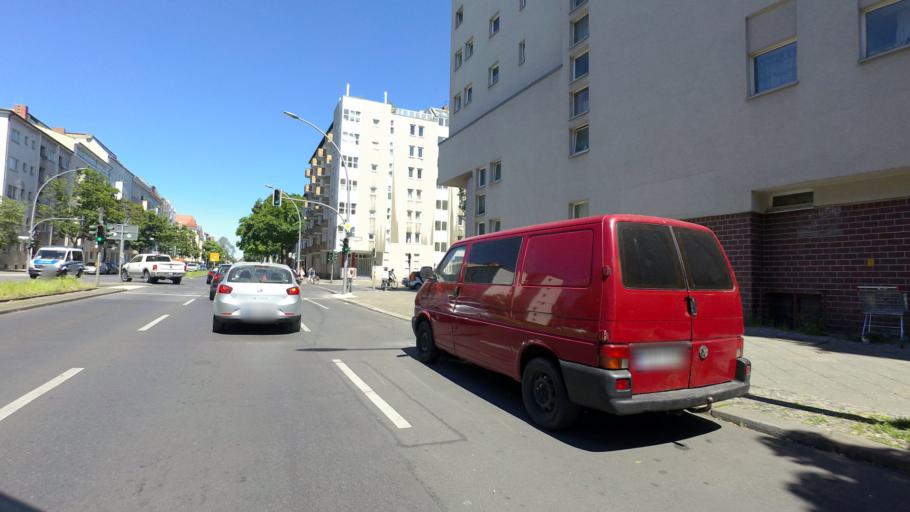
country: DE
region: Berlin
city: Charlottenburg Bezirk
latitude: 52.5095
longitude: 13.3019
